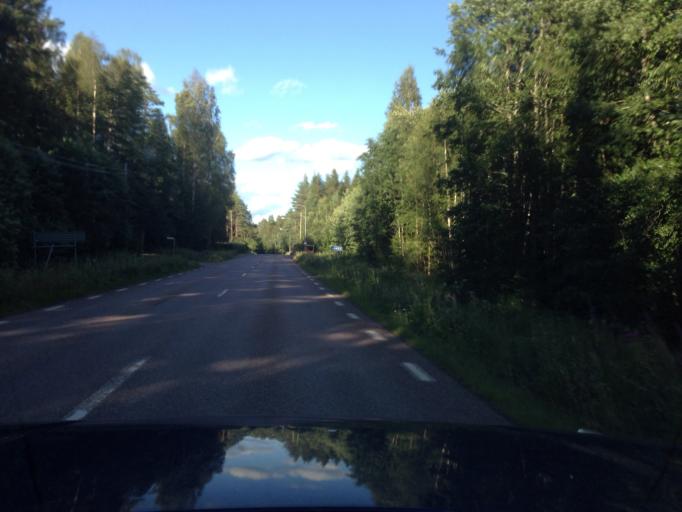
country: SE
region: Dalarna
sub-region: Ludvika Kommun
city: Ludvika
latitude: 60.1432
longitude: 15.0856
